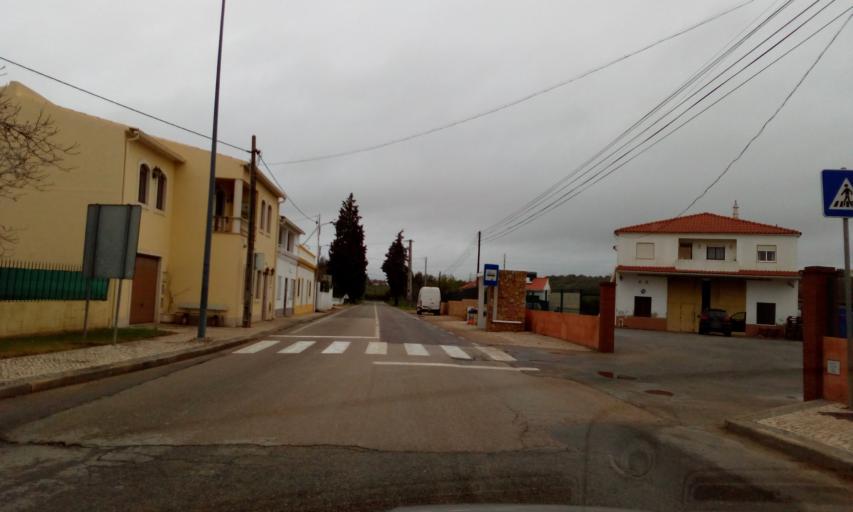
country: PT
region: Faro
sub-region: Albufeira
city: Guia
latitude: 37.1655
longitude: -8.3055
